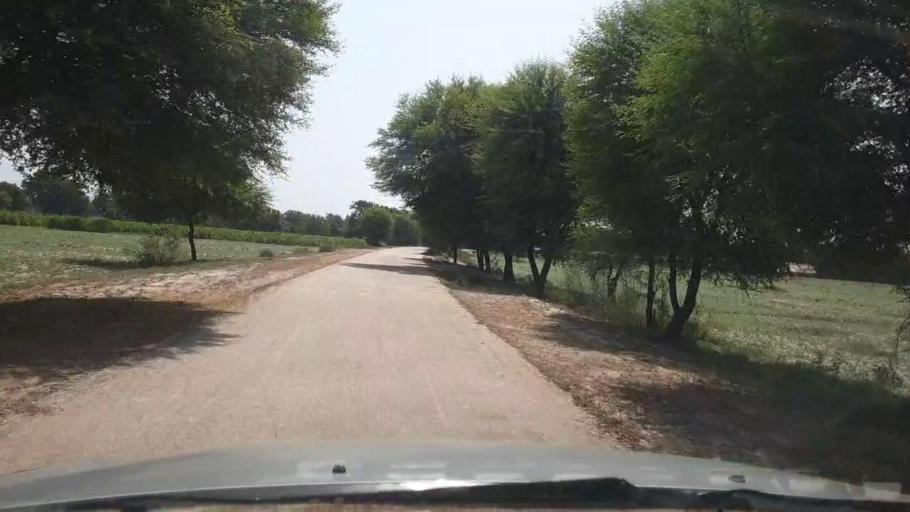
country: PK
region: Sindh
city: Chambar
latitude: 25.2313
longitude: 68.7768
